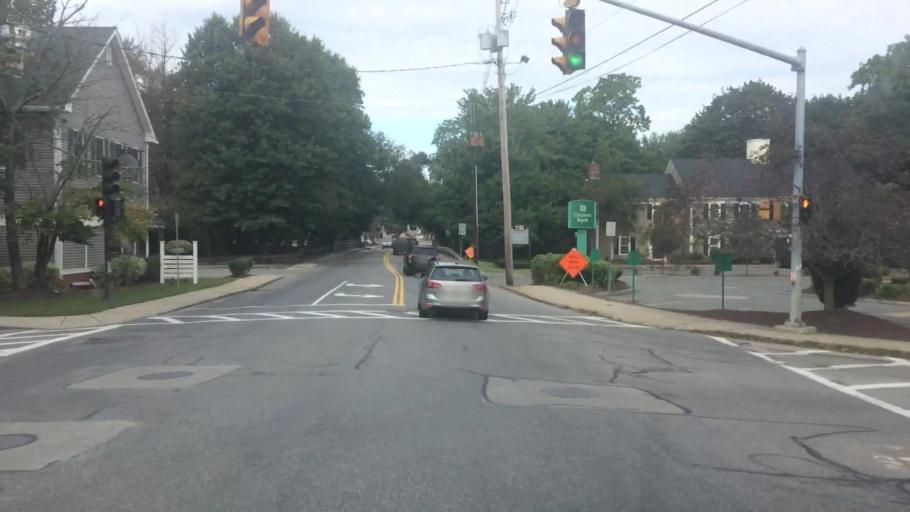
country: US
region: Massachusetts
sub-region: Middlesex County
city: West Concord
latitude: 42.4562
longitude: -71.3875
